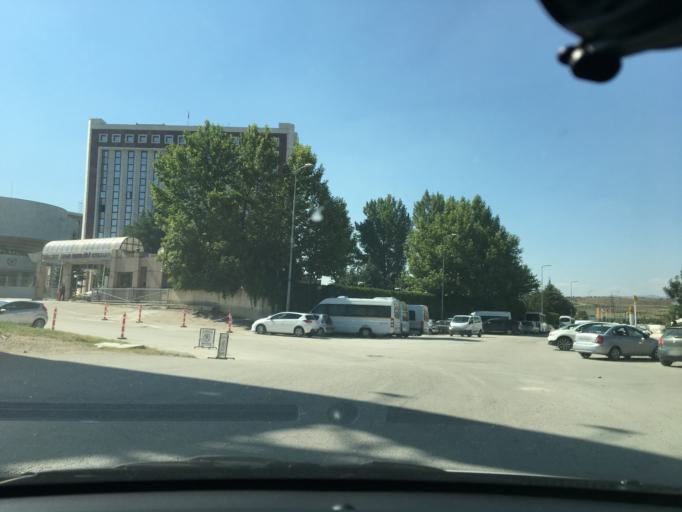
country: TR
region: Ankara
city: Batikent
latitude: 39.9072
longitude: 32.7437
